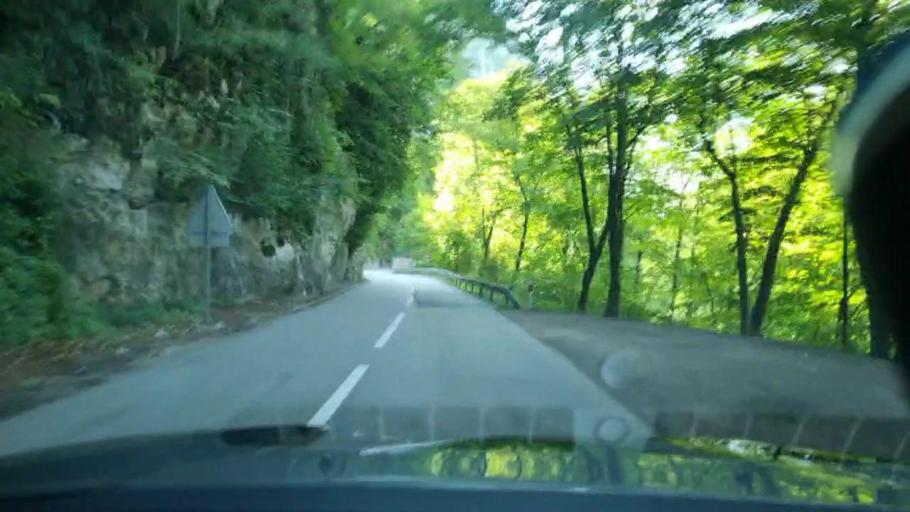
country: BA
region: Federation of Bosnia and Herzegovina
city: Stijena
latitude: 44.8835
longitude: 16.0623
